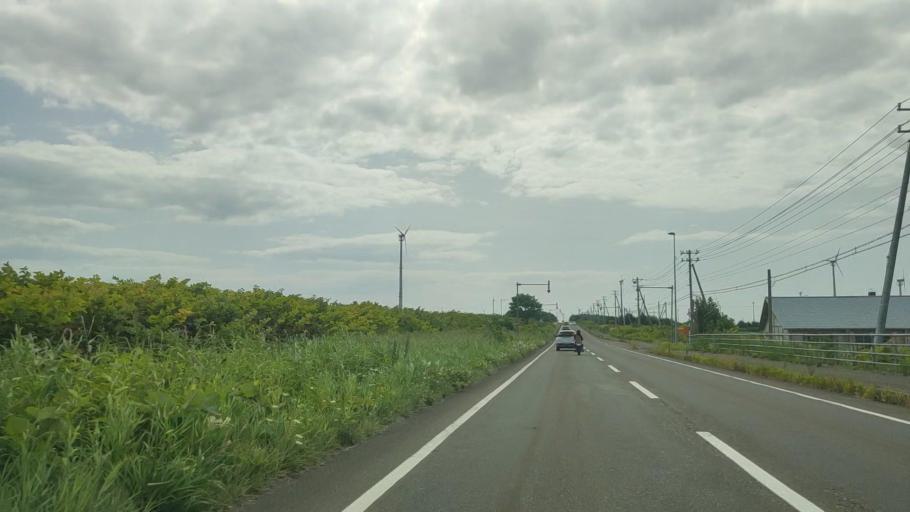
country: JP
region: Hokkaido
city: Rumoi
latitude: 44.4015
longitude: 141.7248
